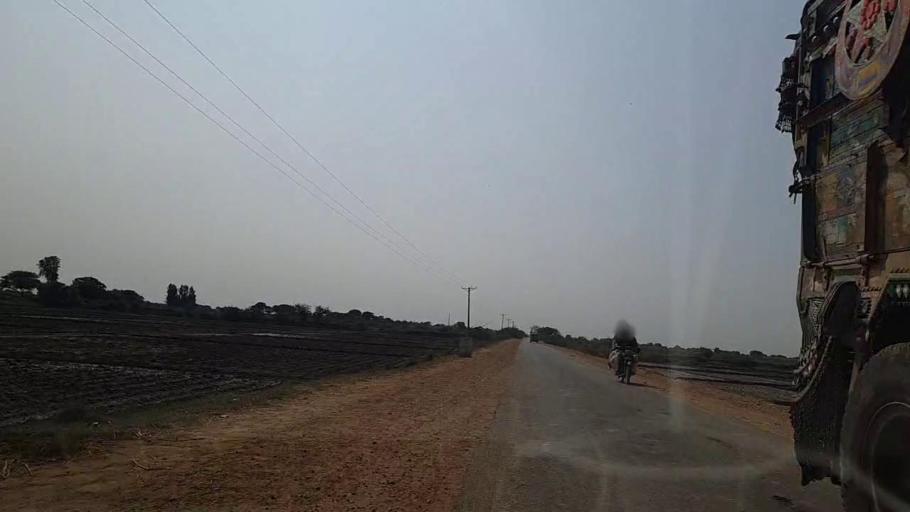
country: PK
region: Sindh
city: Chuhar Jamali
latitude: 24.2807
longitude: 67.9195
